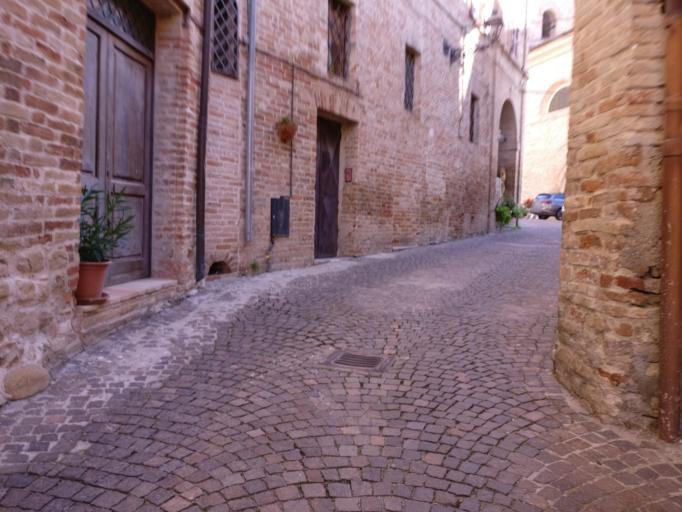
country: IT
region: The Marches
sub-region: Provincia di Ascoli Piceno
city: Montedinove
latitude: 42.9704
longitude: 13.5868
